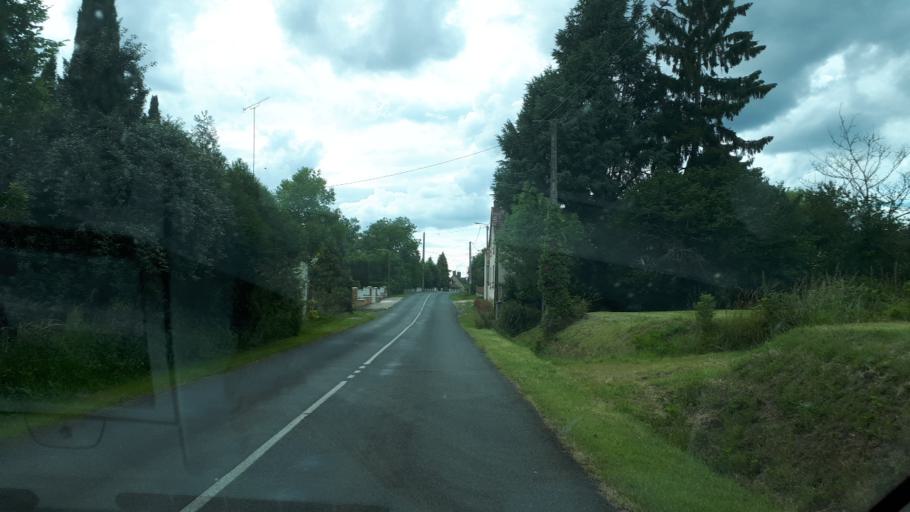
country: FR
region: Centre
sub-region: Departement du Cher
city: Gracay
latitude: 47.1406
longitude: 1.8579
